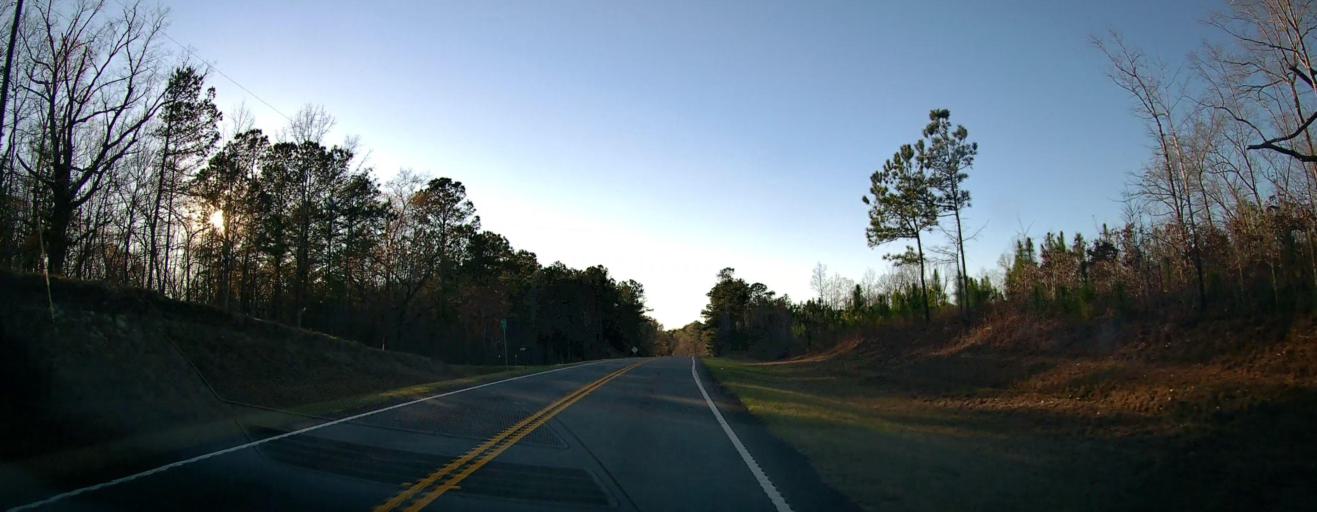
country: US
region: Georgia
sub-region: Talbot County
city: Talbotton
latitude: 32.6585
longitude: -84.6476
